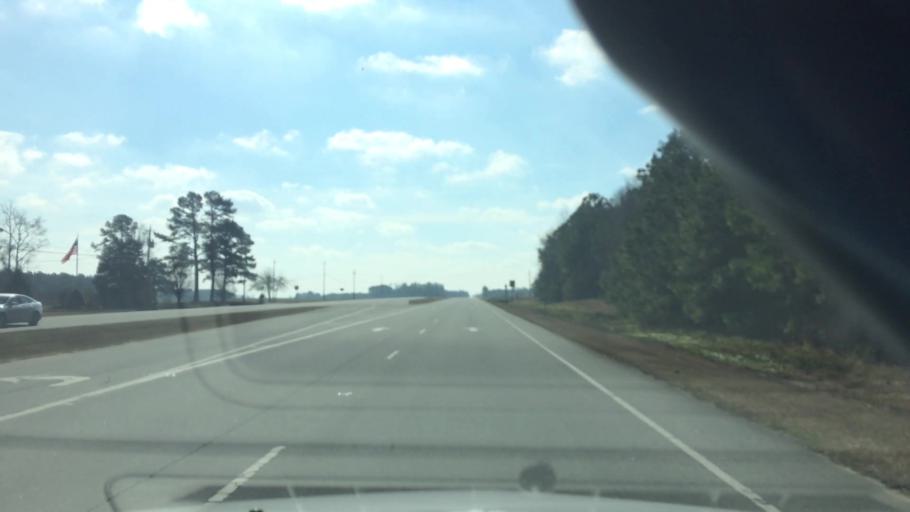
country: US
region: North Carolina
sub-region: Duplin County
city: Beulaville
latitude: 35.1036
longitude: -77.7222
